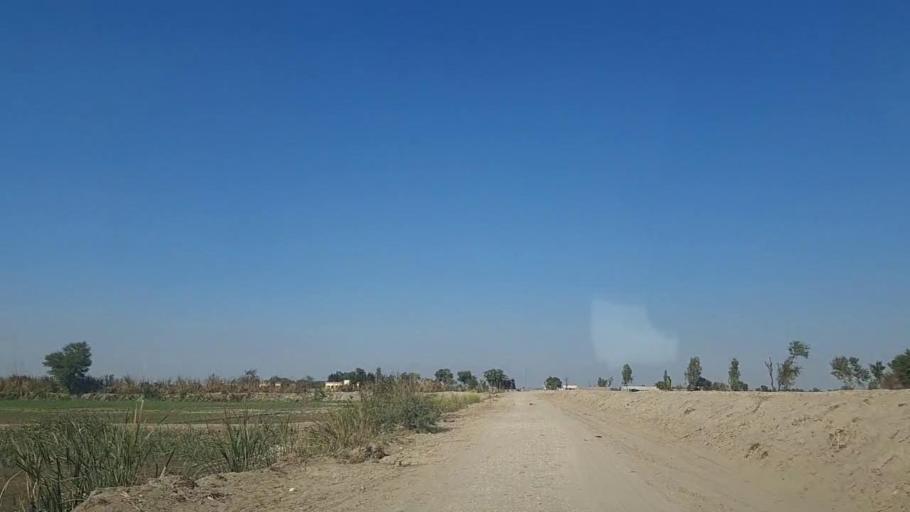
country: PK
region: Sindh
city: Sanghar
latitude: 26.2196
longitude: 68.9291
